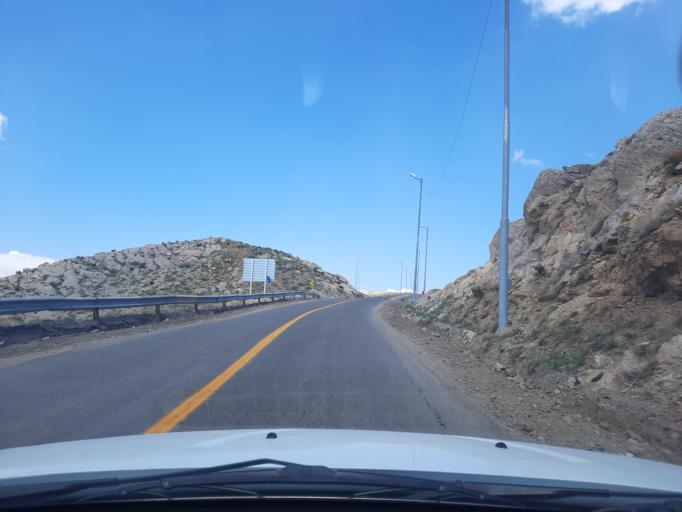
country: IR
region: Qazvin
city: Qazvin
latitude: 36.3810
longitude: 50.2022
